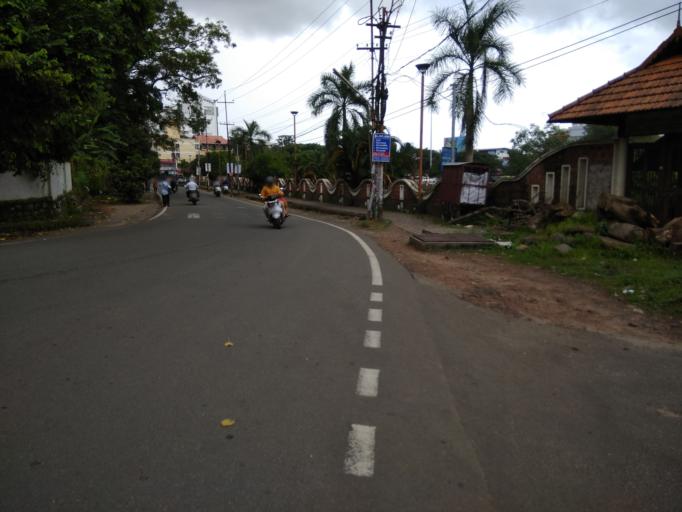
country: IN
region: Kerala
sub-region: Thrissur District
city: Trichur
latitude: 10.5292
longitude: 76.2162
